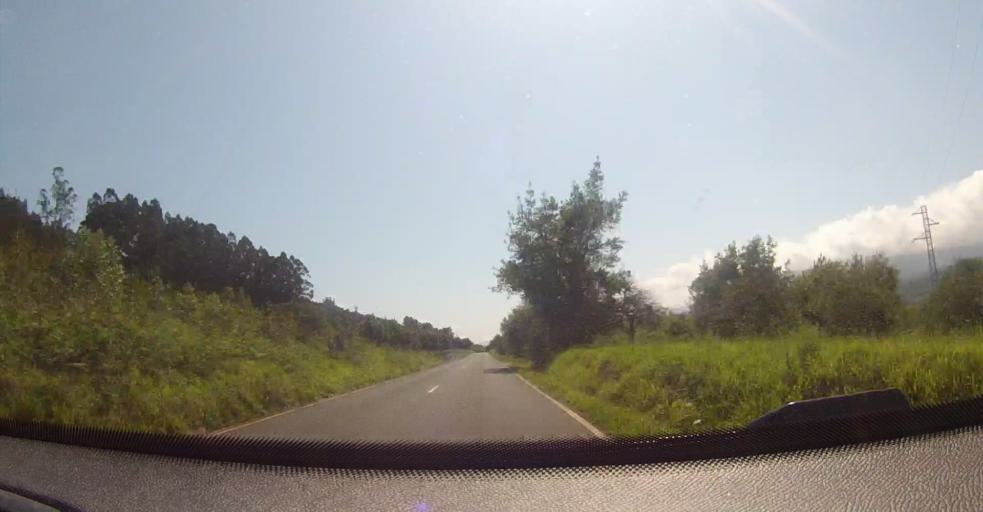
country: ES
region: Asturias
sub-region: Province of Asturias
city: Colunga
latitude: 43.4894
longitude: -5.3088
